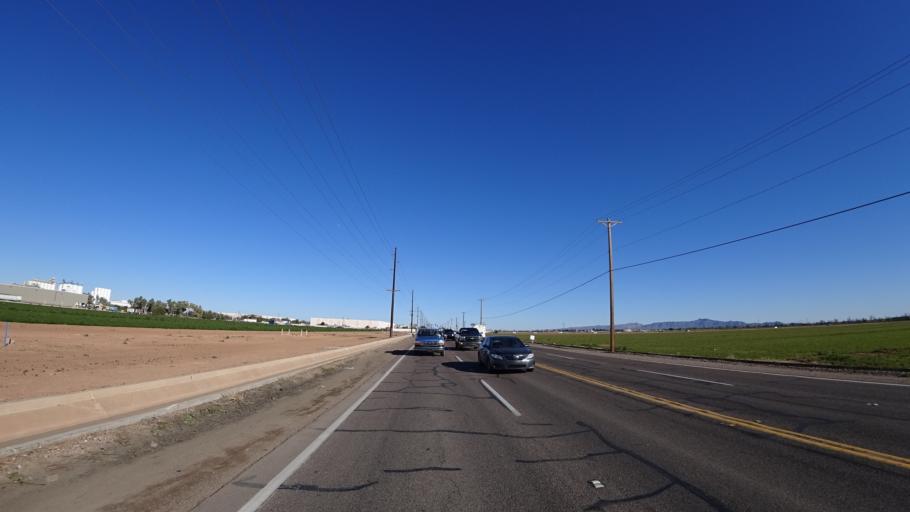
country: US
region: Arizona
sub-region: Maricopa County
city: Tolleson
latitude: 33.4357
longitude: -112.2761
